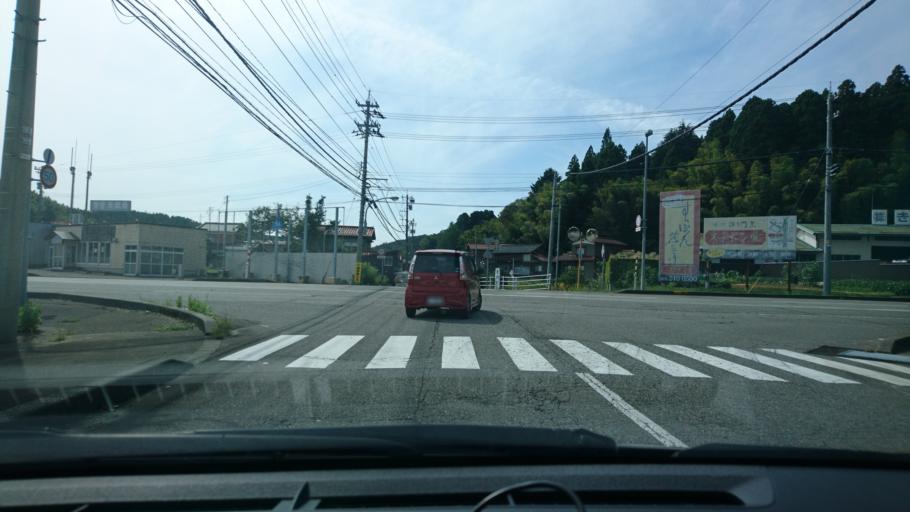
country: JP
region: Fukui
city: Maruoka
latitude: 36.2900
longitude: 136.2958
